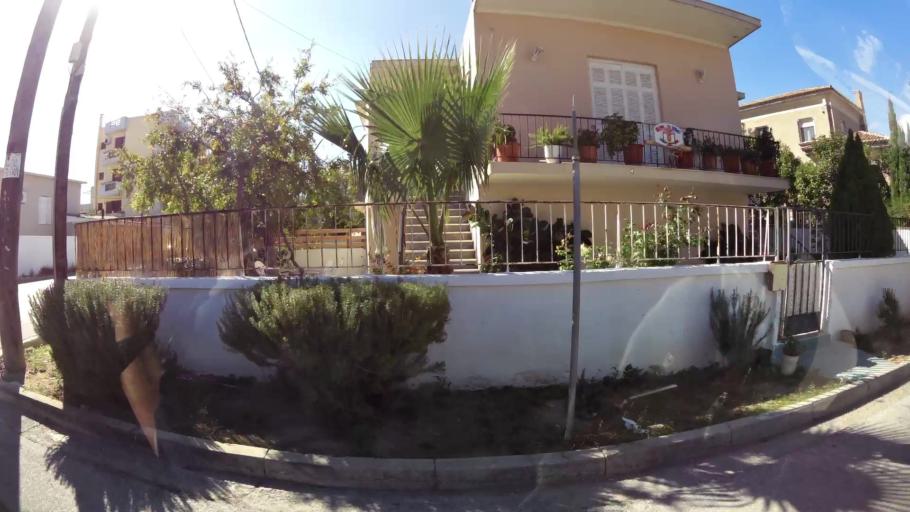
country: GR
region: Attica
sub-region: Nomarchia Anatolikis Attikis
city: Markopoulo
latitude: 37.8783
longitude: 23.9321
